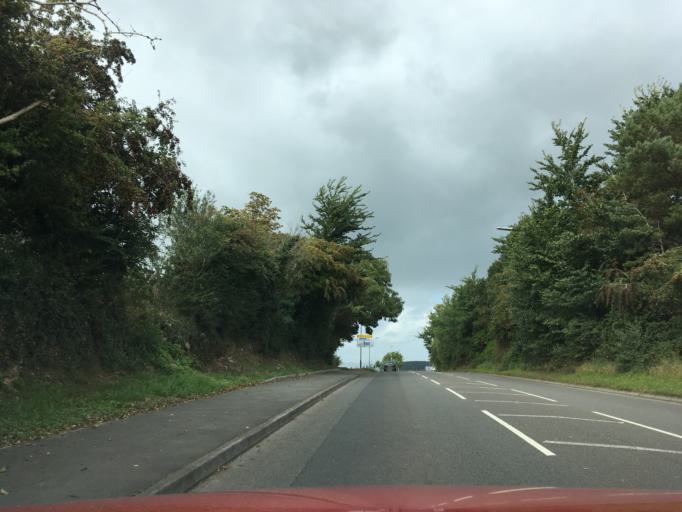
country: GB
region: England
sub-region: South Gloucestershire
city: Thornbury
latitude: 51.6175
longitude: -2.5151
